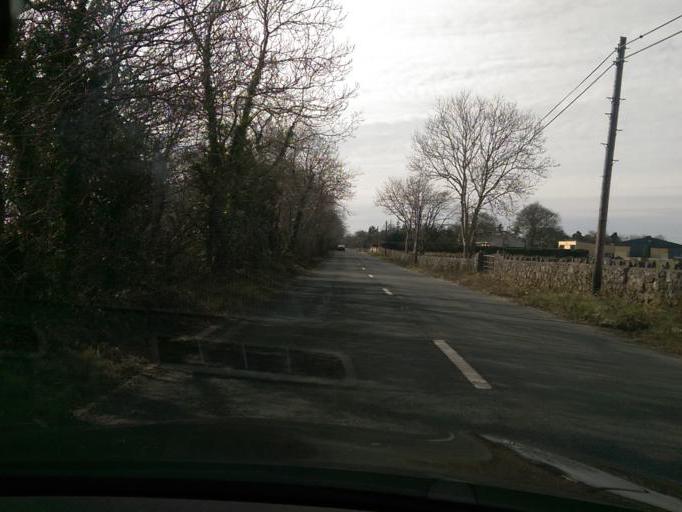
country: IE
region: Connaught
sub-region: County Galway
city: Athenry
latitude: 53.4486
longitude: -8.7086
